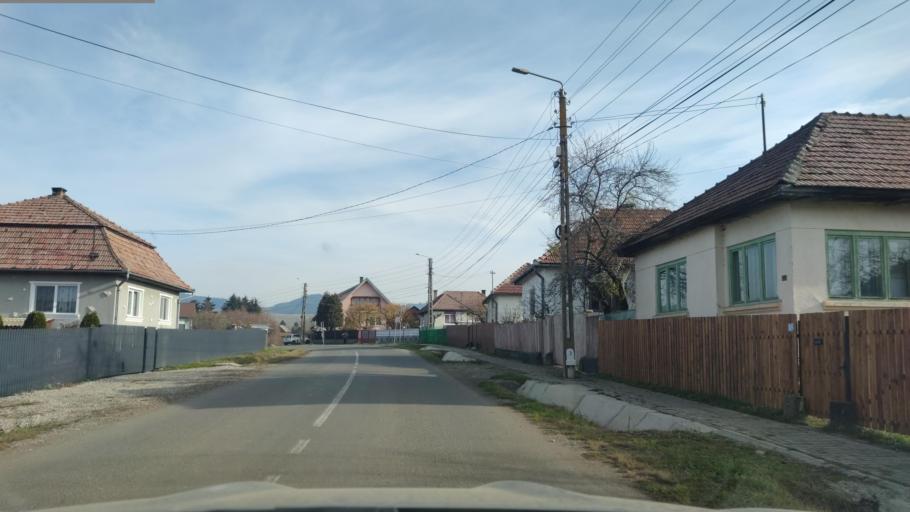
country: RO
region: Harghita
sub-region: Comuna Ditrau
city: Ditrau
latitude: 46.8135
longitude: 25.5201
